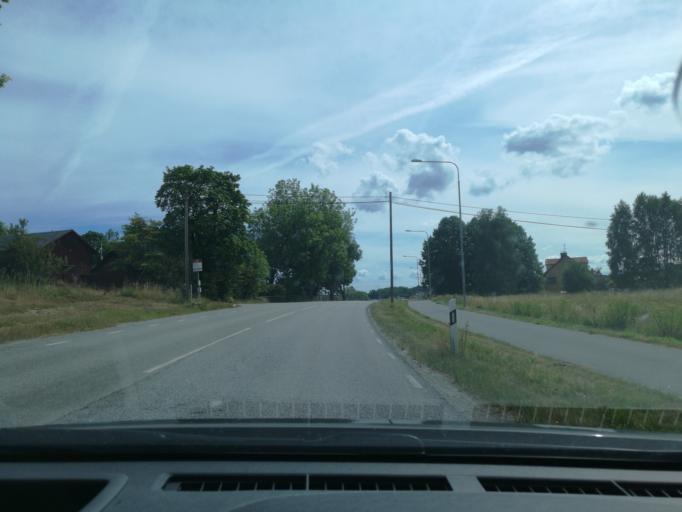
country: SE
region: Stockholm
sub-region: Sigtuna Kommun
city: Rosersberg
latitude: 59.5941
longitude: 17.8892
